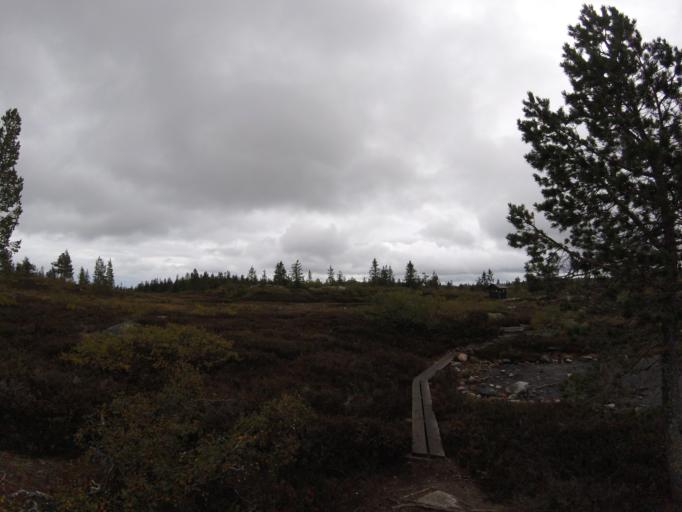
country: NO
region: Buskerud
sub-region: Flesberg
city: Lampeland
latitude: 59.7748
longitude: 9.4033
